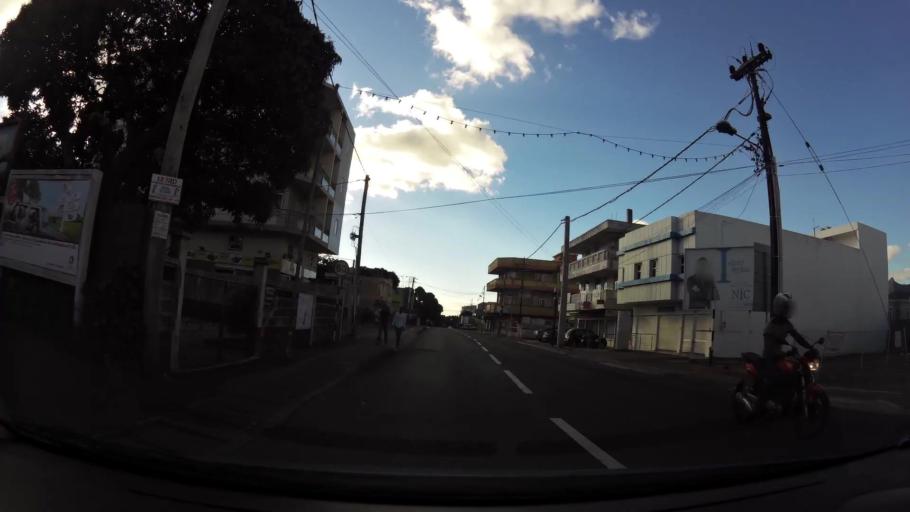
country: MU
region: Plaines Wilhems
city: Ebene
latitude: -20.2382
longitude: 57.4720
